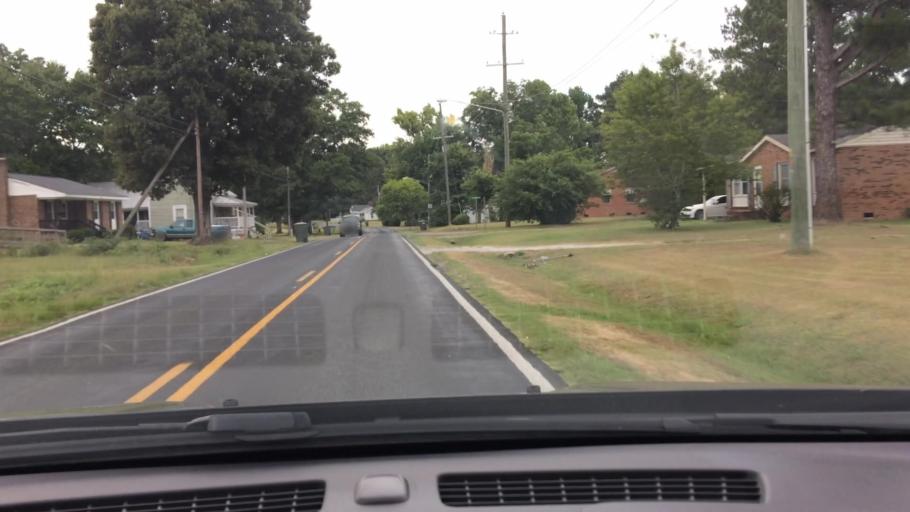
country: US
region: North Carolina
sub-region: Pitt County
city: Ayden
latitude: 35.4620
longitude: -77.4153
